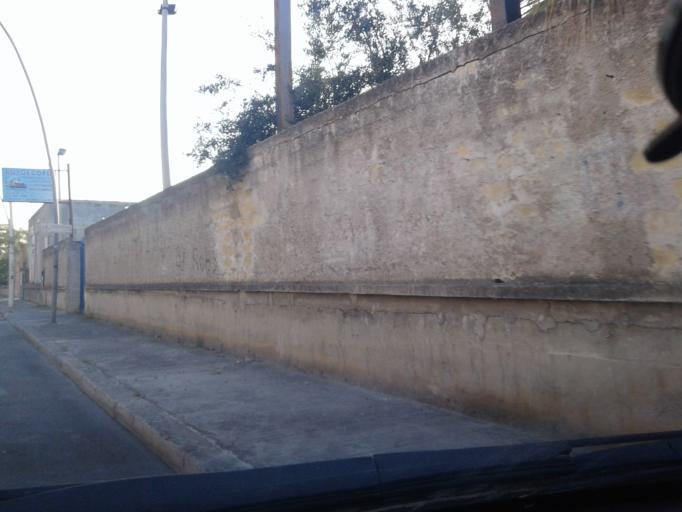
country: IT
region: Sicily
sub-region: Palermo
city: Ciaculli
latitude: 38.0889
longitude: 13.3608
